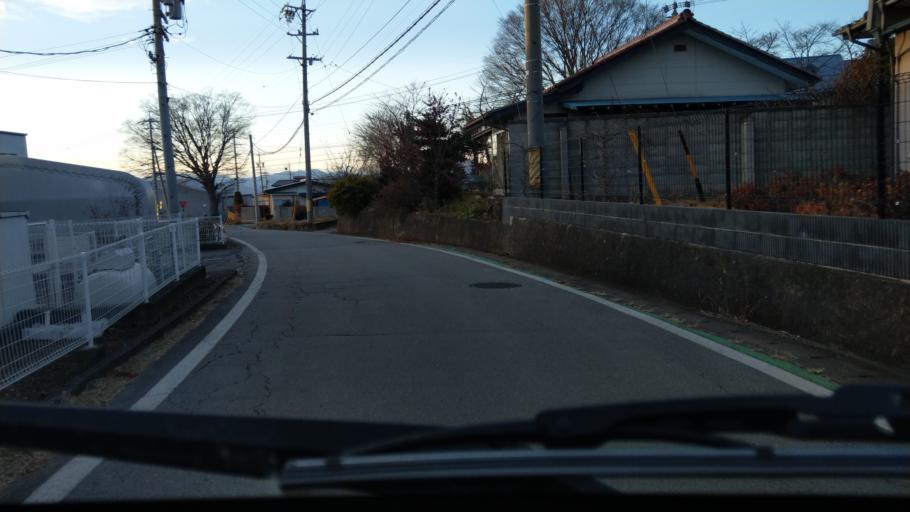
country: JP
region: Nagano
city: Komoro
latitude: 36.3440
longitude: 138.3891
